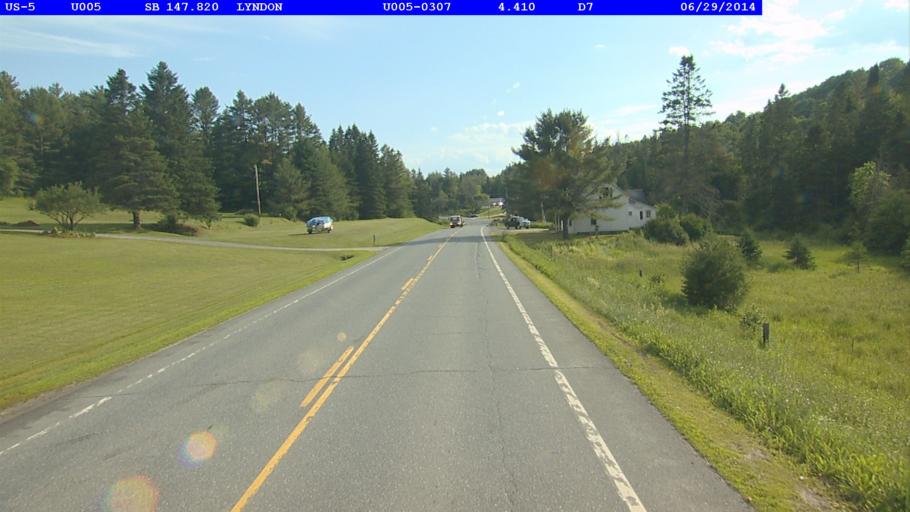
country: US
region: Vermont
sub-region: Caledonia County
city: Lyndonville
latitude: 44.5535
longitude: -71.9999
